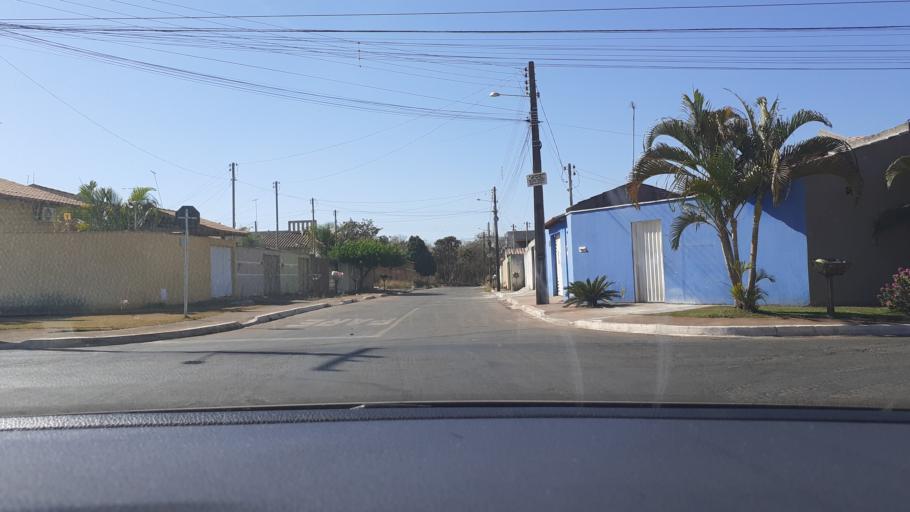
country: BR
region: Goias
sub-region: Aparecida De Goiania
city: Aparecida de Goiania
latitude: -16.8431
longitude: -49.2497
